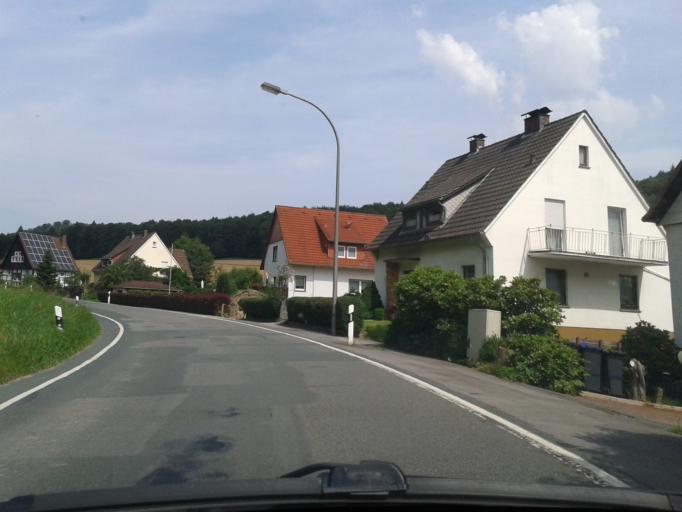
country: DE
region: North Rhine-Westphalia
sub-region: Regierungsbezirk Detmold
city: Blomberg
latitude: 51.9308
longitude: 9.1525
